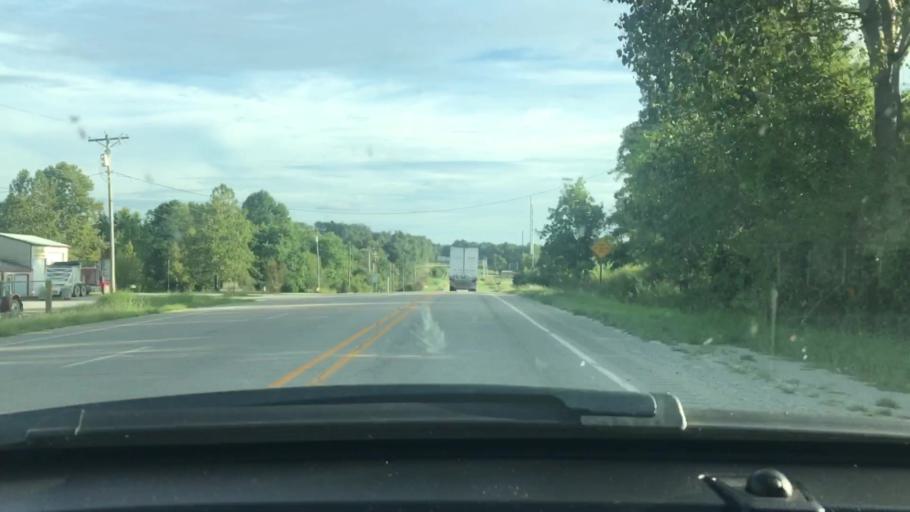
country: US
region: Arkansas
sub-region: Lawrence County
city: Hoxie
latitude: 36.1405
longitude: -91.1581
